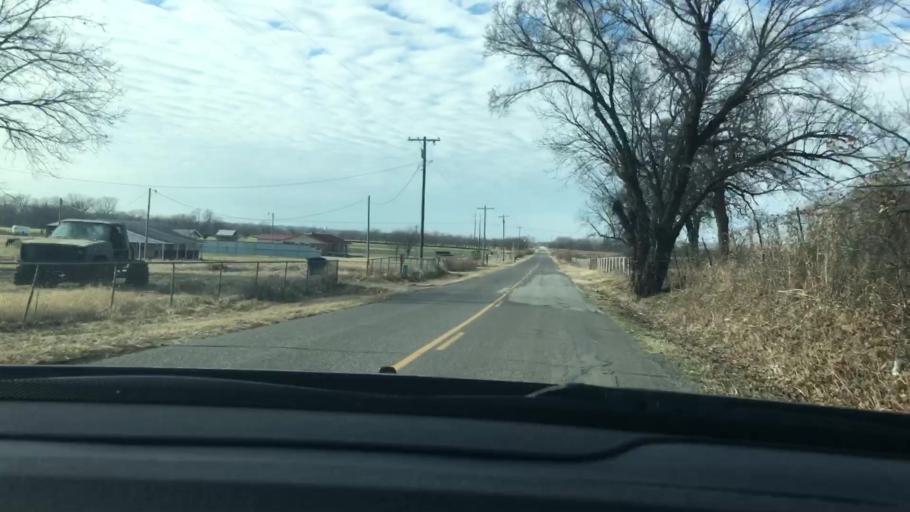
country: US
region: Oklahoma
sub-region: Garvin County
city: Pauls Valley
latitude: 34.7386
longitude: -97.1528
